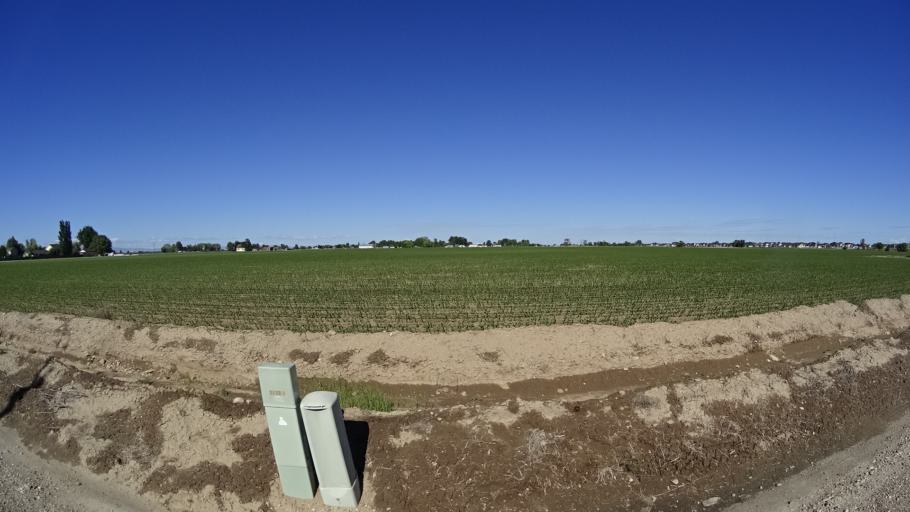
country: US
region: Idaho
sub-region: Ada County
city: Star
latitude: 43.6397
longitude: -116.4534
